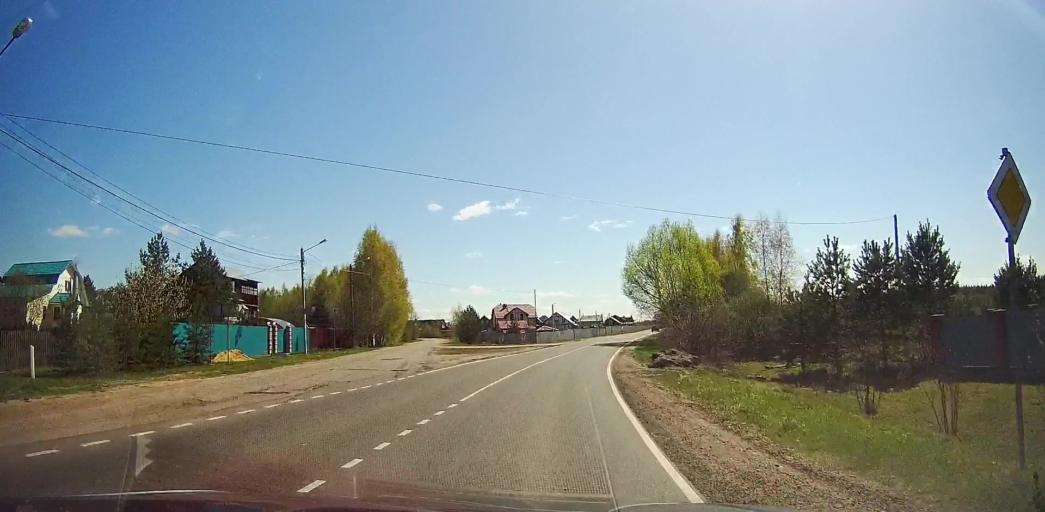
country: RU
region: Moskovskaya
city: Rechitsy
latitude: 55.5352
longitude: 38.4275
